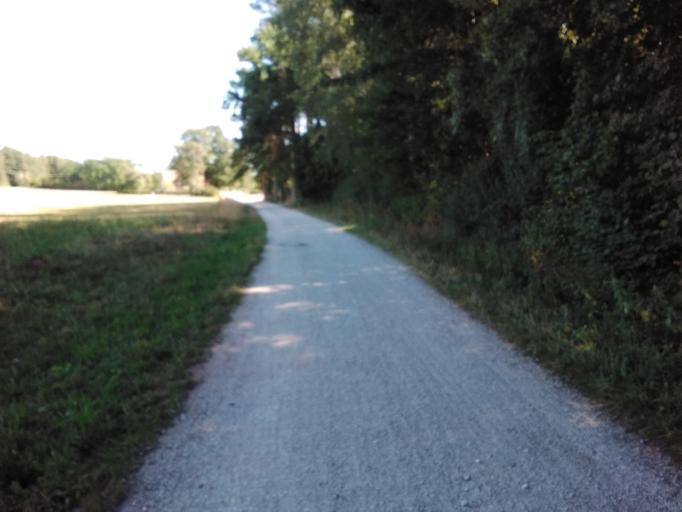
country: DE
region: Bavaria
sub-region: Regierungsbezirk Mittelfranken
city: Allersberg
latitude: 49.2374
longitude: 11.2036
